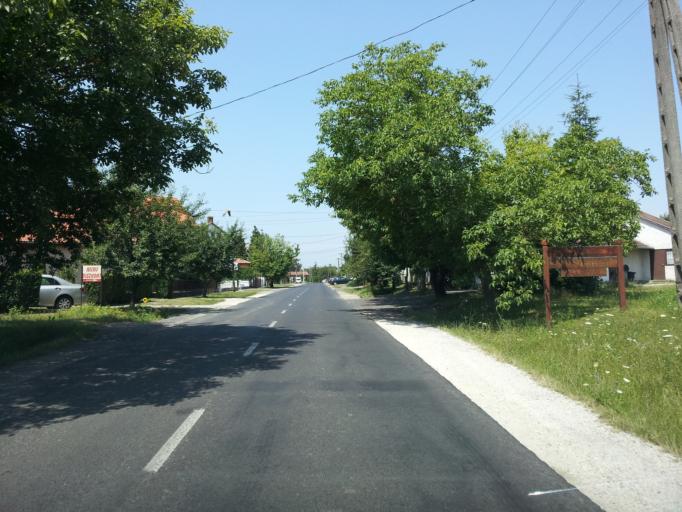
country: HU
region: Zala
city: Zalaegerszeg
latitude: 46.8613
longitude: 16.8102
